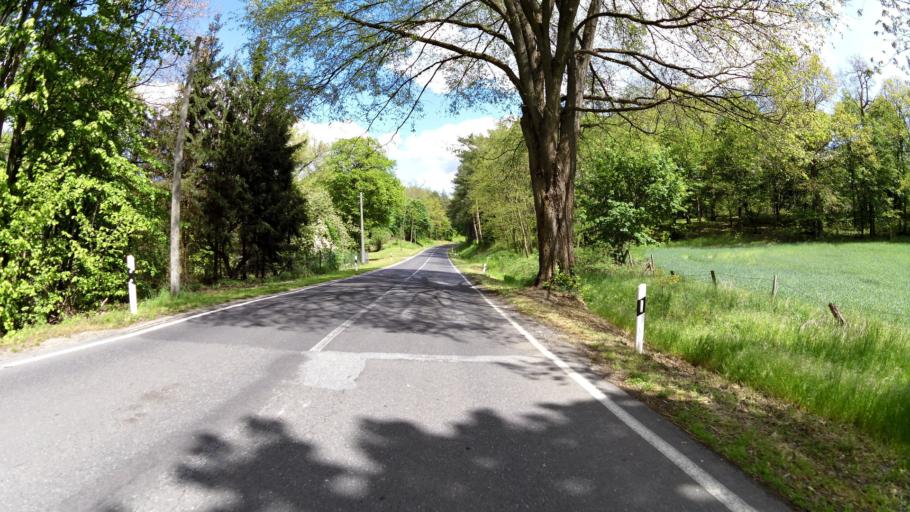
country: DE
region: Brandenburg
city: Diensdorf-Radlow
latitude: 52.1866
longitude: 14.0845
